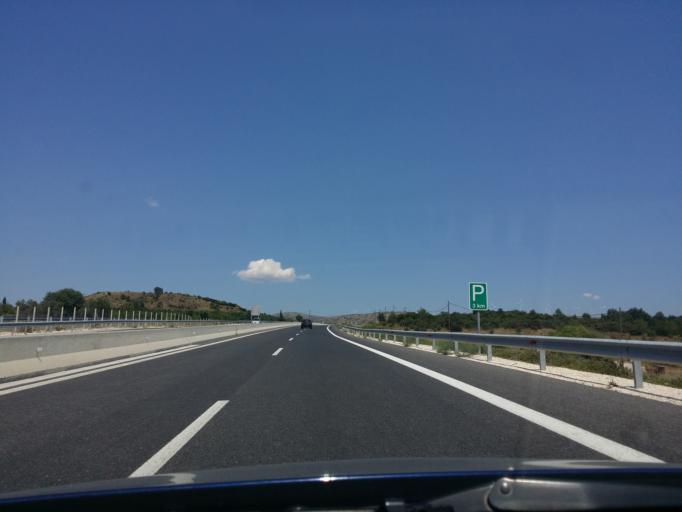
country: GR
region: Peloponnese
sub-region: Nomos Arkadias
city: Megalopoli
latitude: 37.3868
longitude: 22.2754
